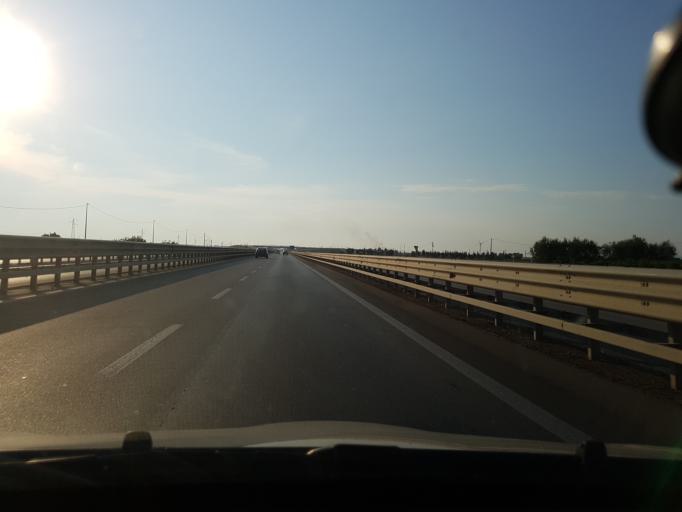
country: IT
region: Apulia
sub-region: Provincia di Foggia
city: Orta Nova
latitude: 41.3392
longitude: 15.7496
